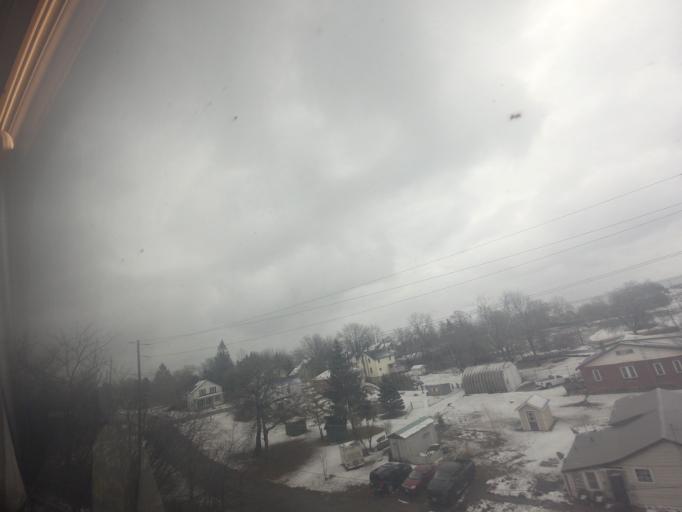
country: CA
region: Ontario
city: Cobourg
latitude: 43.9471
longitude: -78.2913
